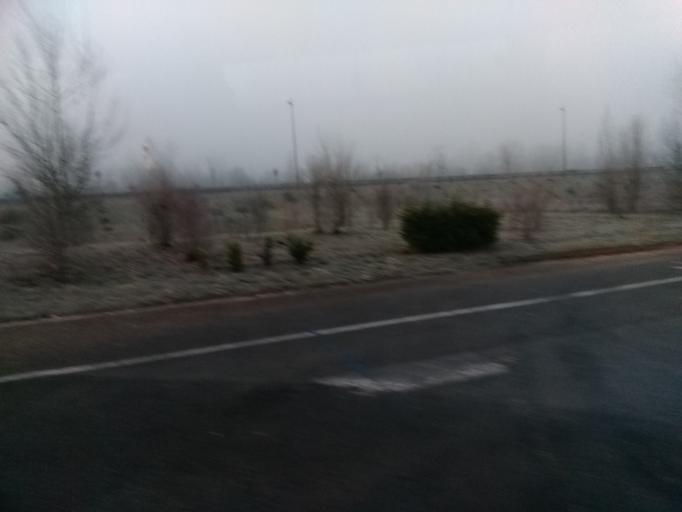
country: FR
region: Aquitaine
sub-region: Departement de la Dordogne
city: Terrasson-Lavilledieu
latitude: 45.1320
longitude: 1.2765
